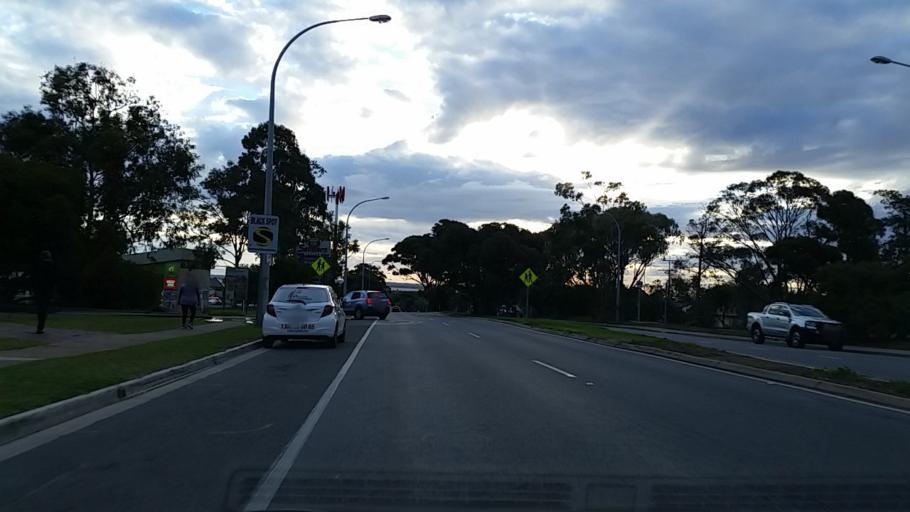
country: AU
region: South Australia
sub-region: Salisbury
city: Ingle Farm
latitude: -34.8288
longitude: 138.6512
